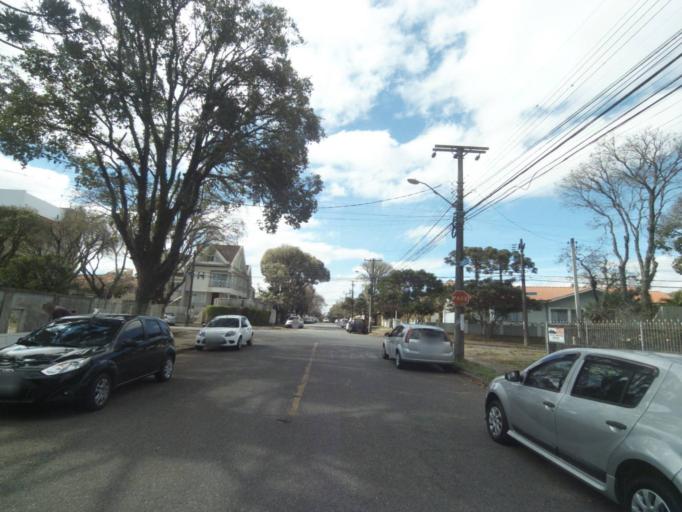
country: BR
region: Parana
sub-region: Curitiba
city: Curitiba
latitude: -25.4695
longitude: -49.2861
